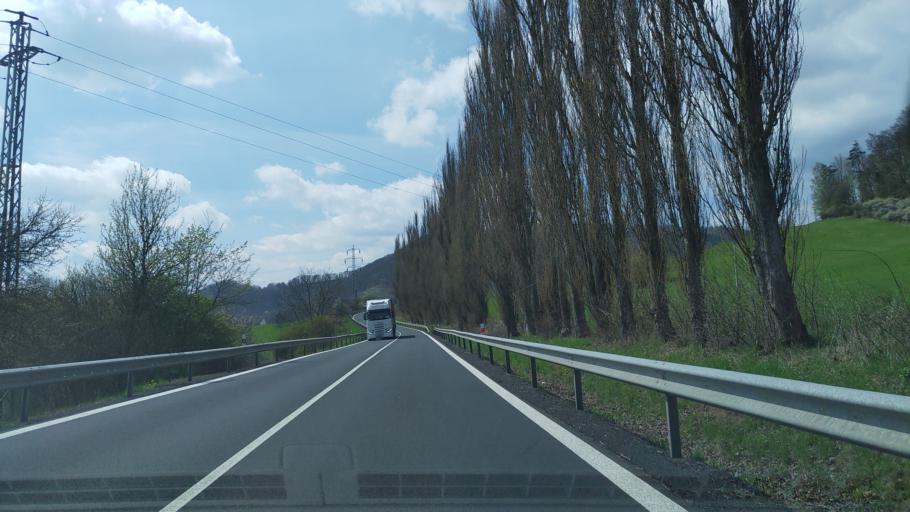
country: CZ
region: Karlovarsky
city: Ostrov
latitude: 50.3332
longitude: 13.0289
